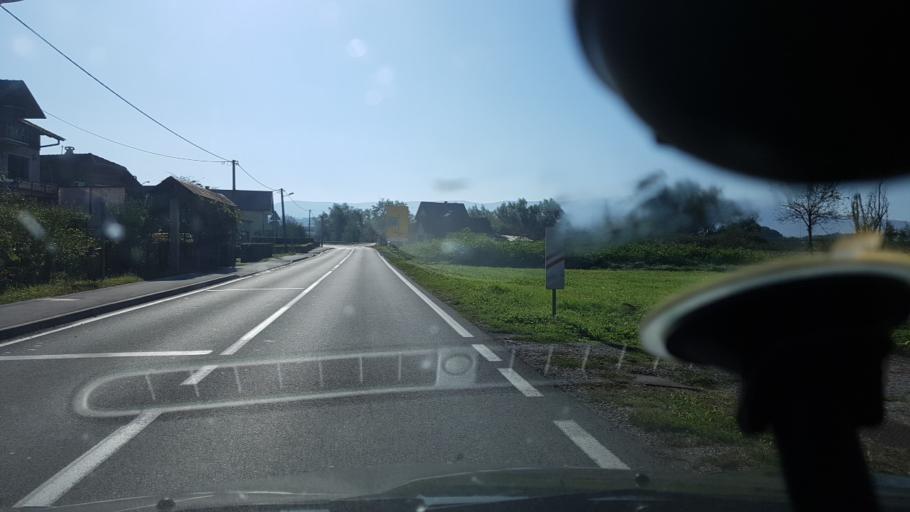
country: HR
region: Krapinsko-Zagorska
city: Zabok
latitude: 46.0197
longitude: 15.9294
